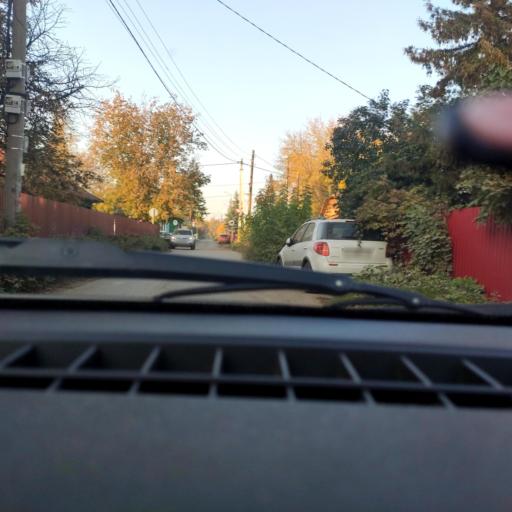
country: RU
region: Bashkortostan
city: Ufa
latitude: 54.7981
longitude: 56.1465
